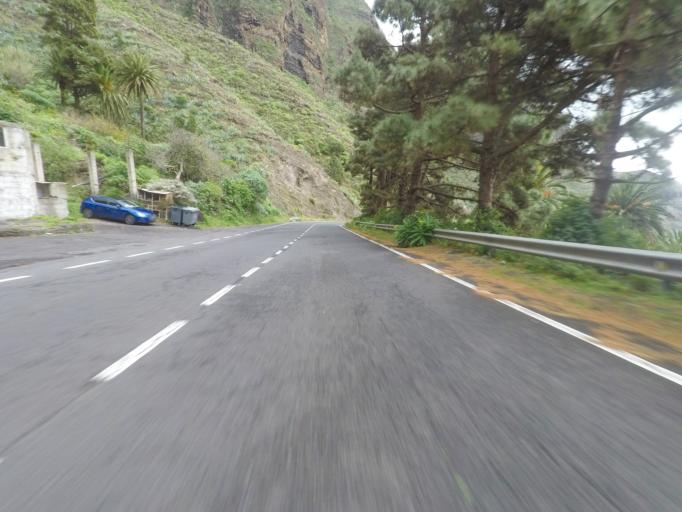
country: ES
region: Canary Islands
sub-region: Provincia de Santa Cruz de Tenerife
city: Hermigua
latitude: 28.1323
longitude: -17.1826
